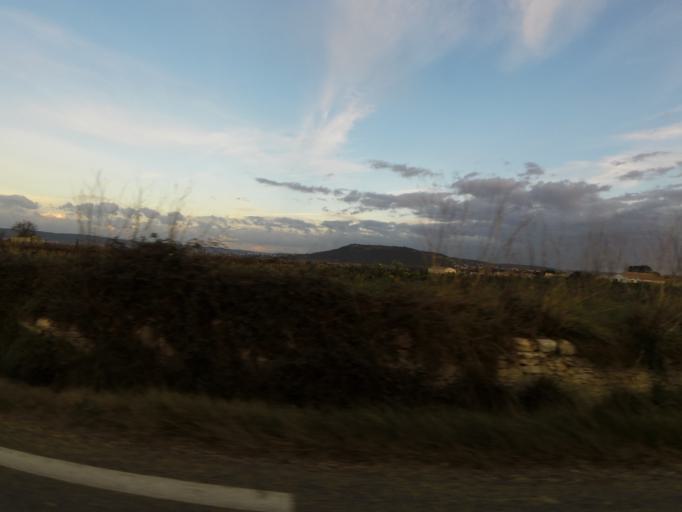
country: FR
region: Languedoc-Roussillon
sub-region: Departement du Gard
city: Calvisson
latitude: 43.7921
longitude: 4.1951
